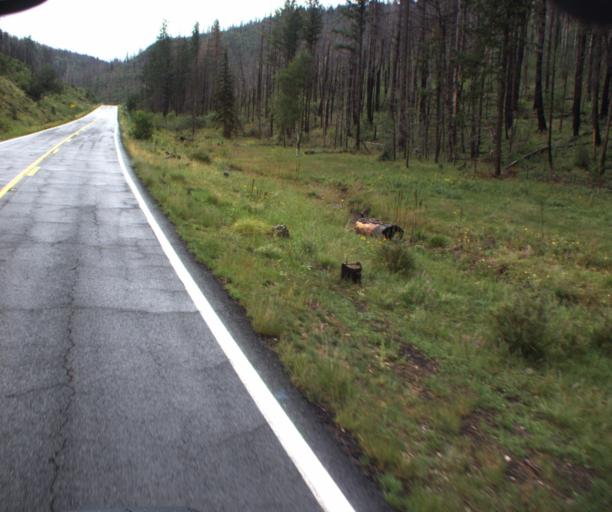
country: US
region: Arizona
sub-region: Apache County
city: Eagar
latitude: 33.7913
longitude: -109.1632
